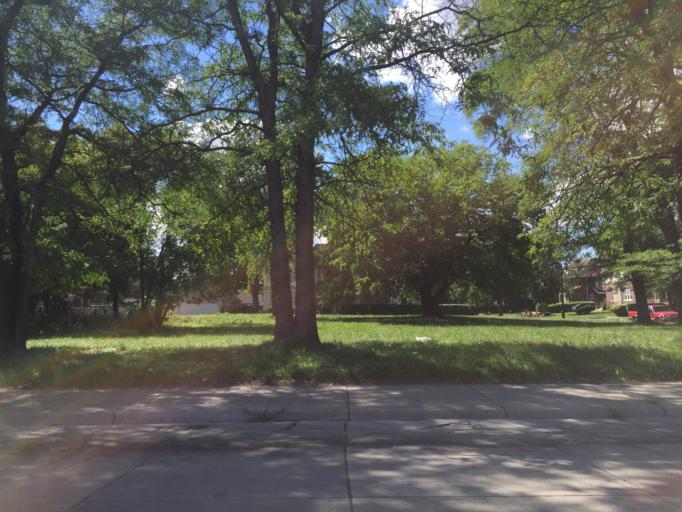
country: US
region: Michigan
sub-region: Wayne County
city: Highland Park
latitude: 42.3845
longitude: -83.0829
